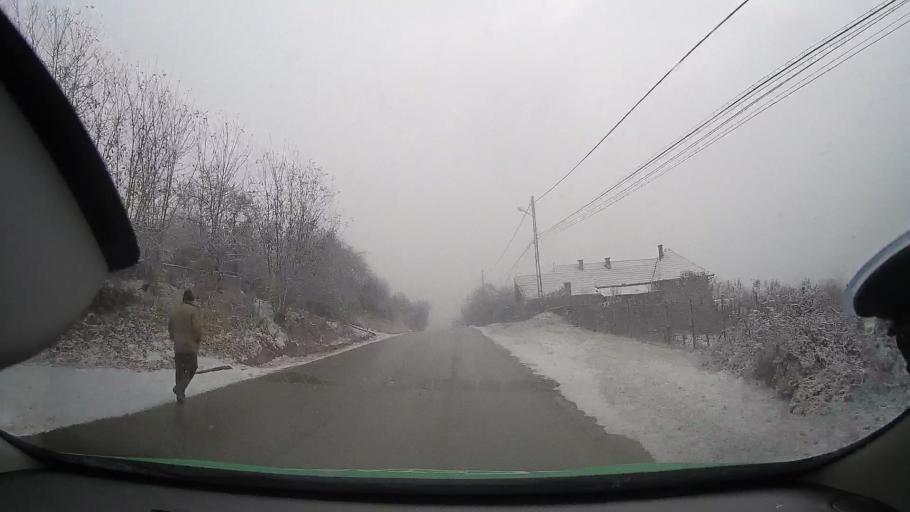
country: RO
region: Alba
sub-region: Comuna Lopadea Noua
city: Lopadea Noua
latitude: 46.2936
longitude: 23.8172
